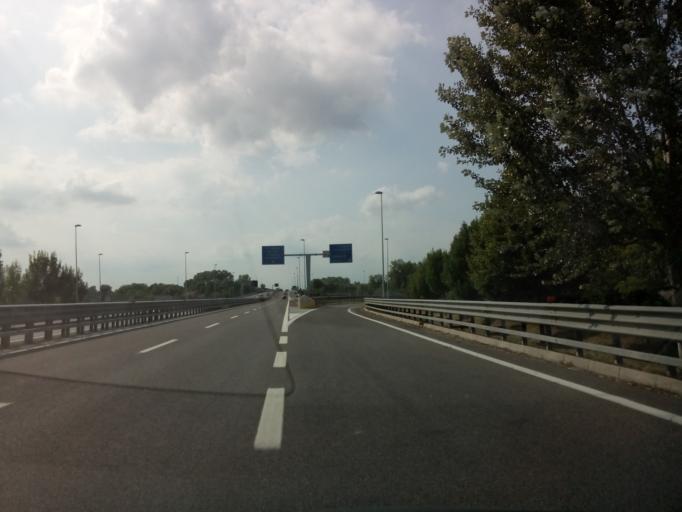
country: IT
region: Veneto
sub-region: Provincia di Padova
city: Limena
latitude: 45.4587
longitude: 11.8401
